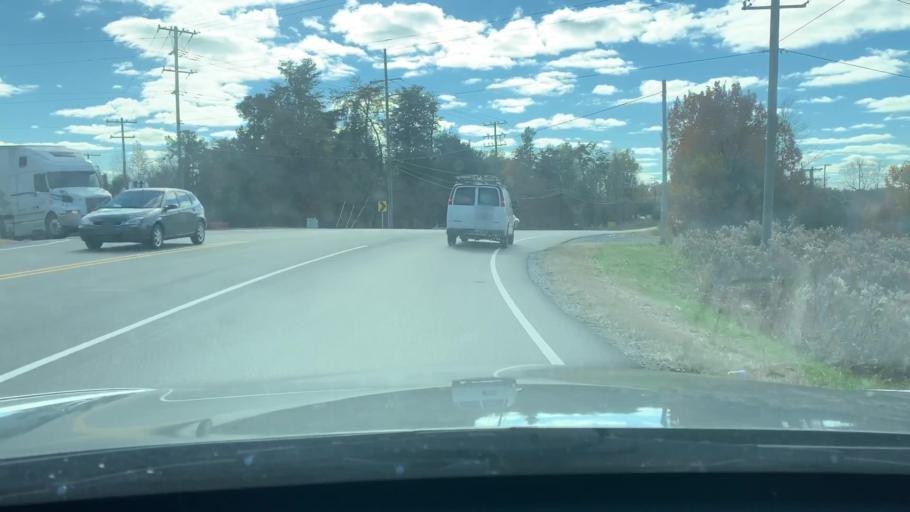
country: US
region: North Carolina
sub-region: Alamance County
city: Haw River
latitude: 36.0786
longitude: -79.3483
